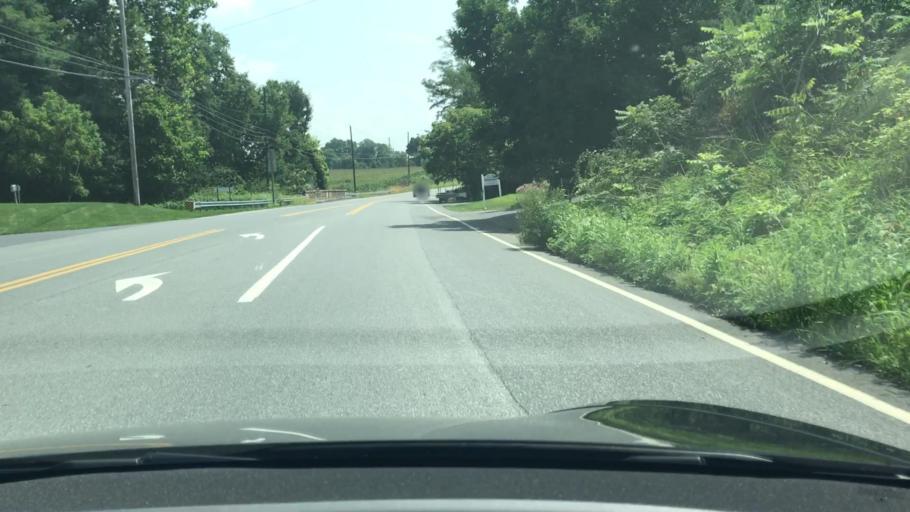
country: US
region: Pennsylvania
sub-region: Lancaster County
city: Salunga
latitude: 40.1097
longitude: -76.4514
